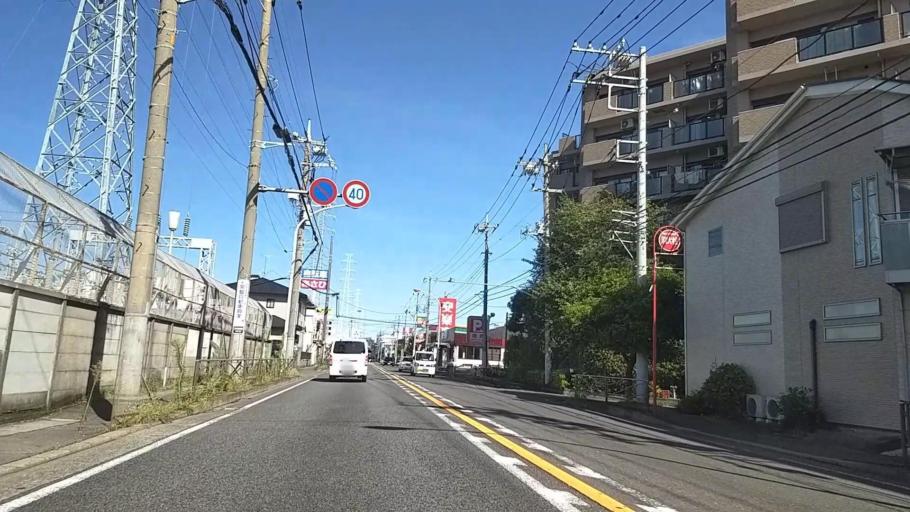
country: JP
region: Kanagawa
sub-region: Kawasaki-shi
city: Kawasaki
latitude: 35.5674
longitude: 139.6376
